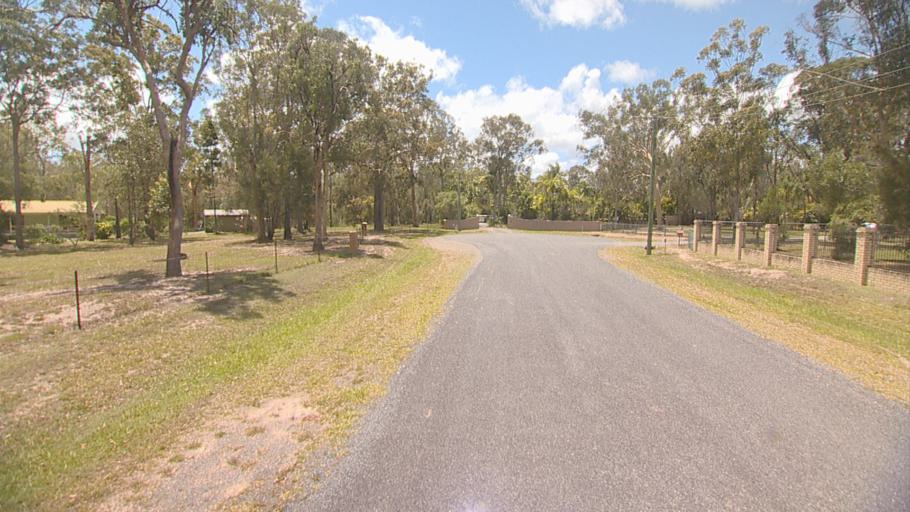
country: AU
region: Queensland
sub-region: Gold Coast
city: Yatala
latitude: -27.6826
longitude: 153.2779
